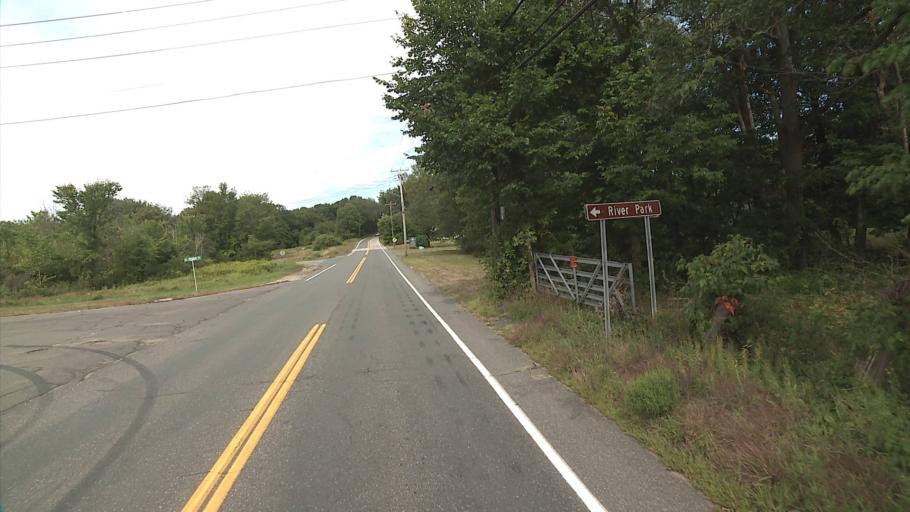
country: US
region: Connecticut
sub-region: Tolland County
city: South Coventry
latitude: 41.8002
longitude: -72.2979
